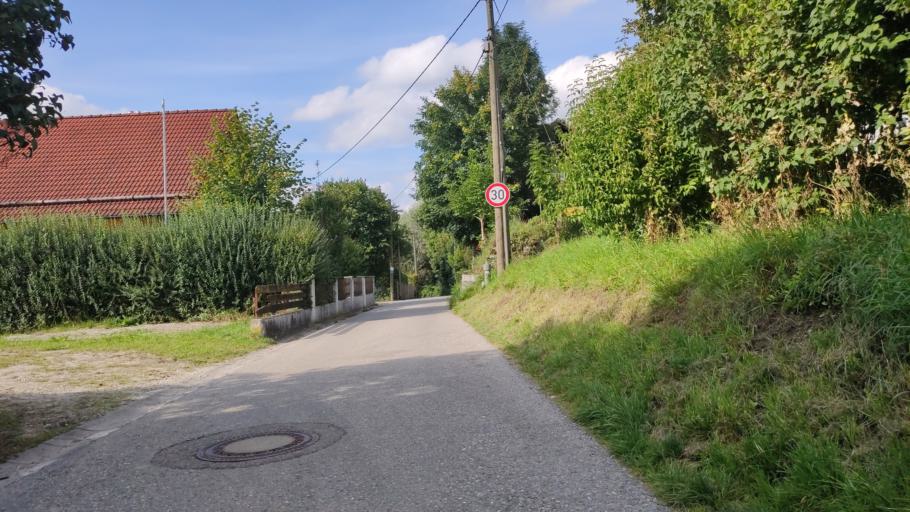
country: DE
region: Bavaria
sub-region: Upper Bavaria
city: Kaufering
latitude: 48.0943
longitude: 10.8741
